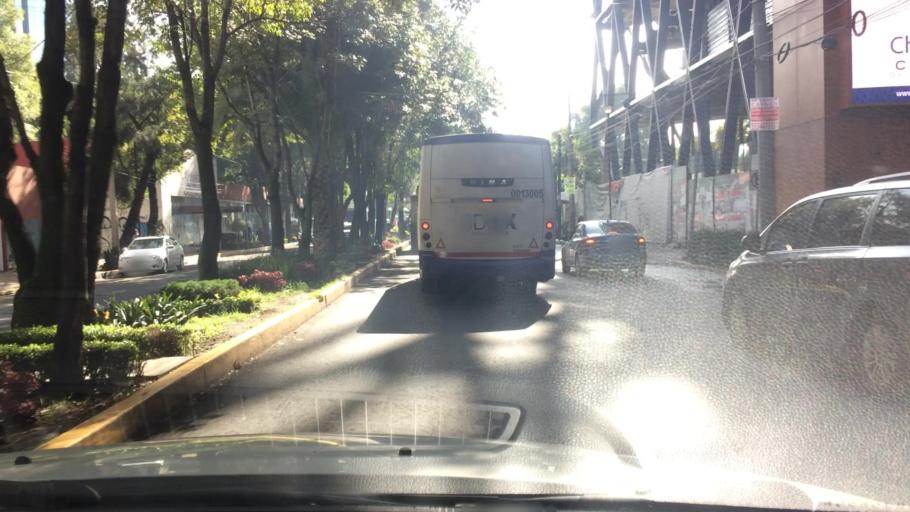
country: MX
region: Mexico City
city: Alvaro Obregon
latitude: 19.3499
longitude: -99.1877
